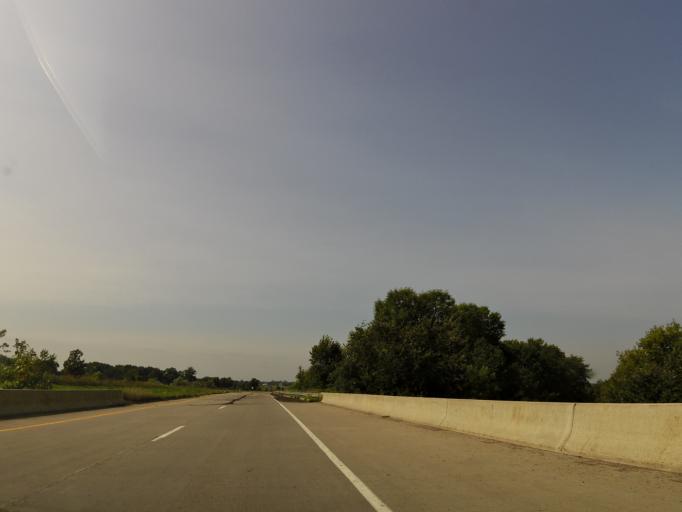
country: US
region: Minnesota
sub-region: Carver County
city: Norwood (historical)
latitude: 44.7708
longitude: -93.9540
